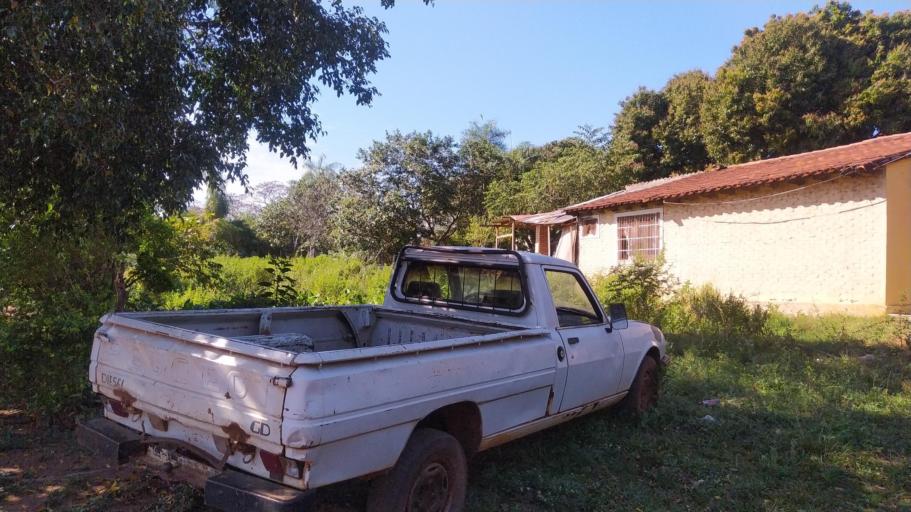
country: PY
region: Misiones
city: San Juan Bautista
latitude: -26.6654
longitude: -57.1347
